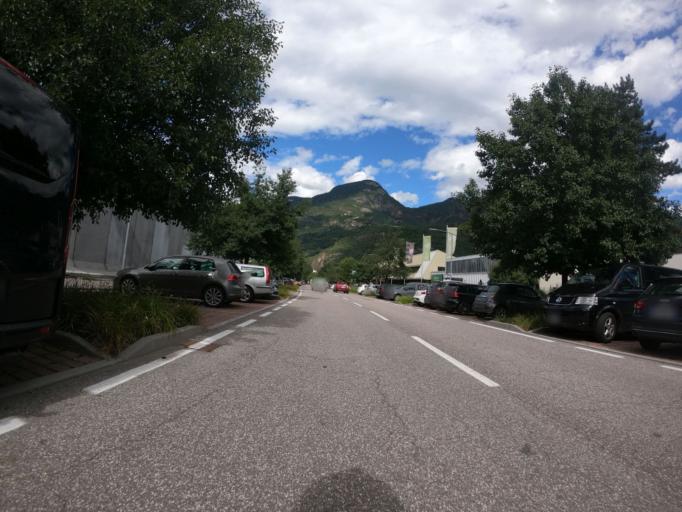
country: IT
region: Trentino-Alto Adige
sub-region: Bolzano
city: Sinigo
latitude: 46.6303
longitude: 11.1687
